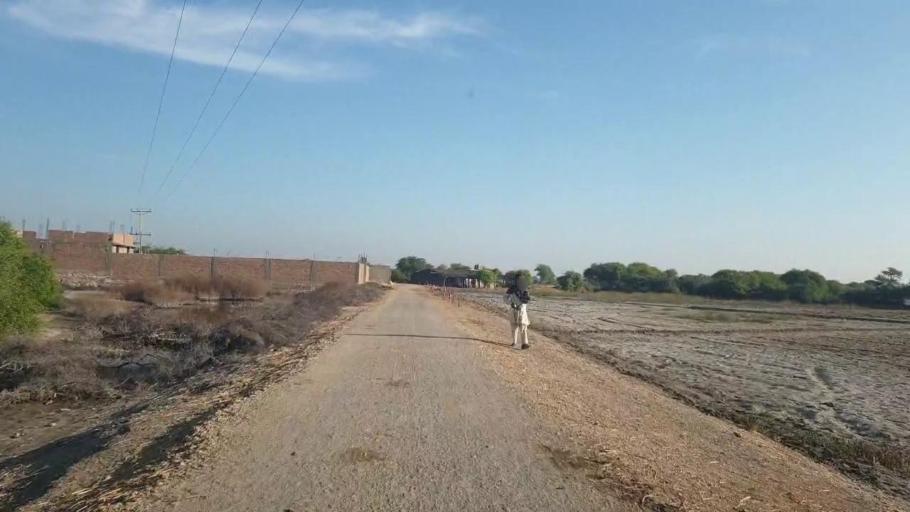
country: PK
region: Sindh
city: Talhar
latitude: 24.8153
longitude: 68.8395
